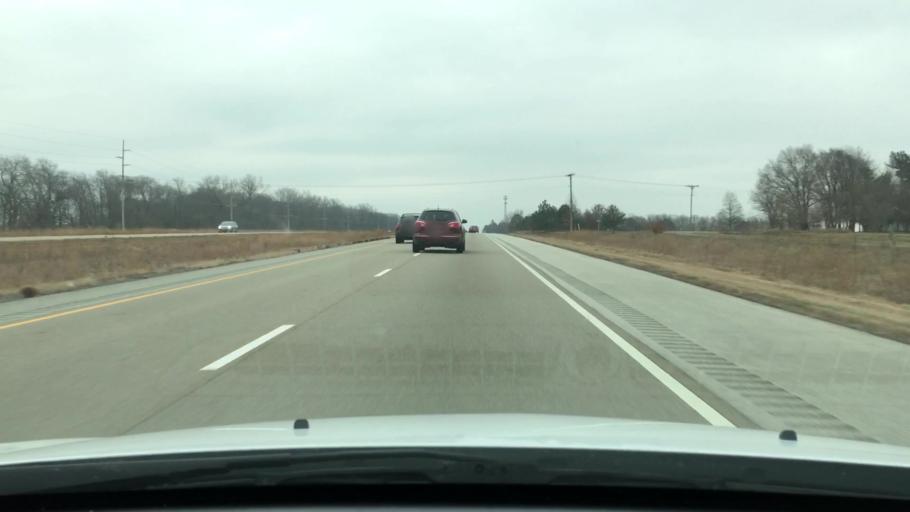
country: US
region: Illinois
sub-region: Logan County
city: Atlanta
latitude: 40.2364
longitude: -89.2593
